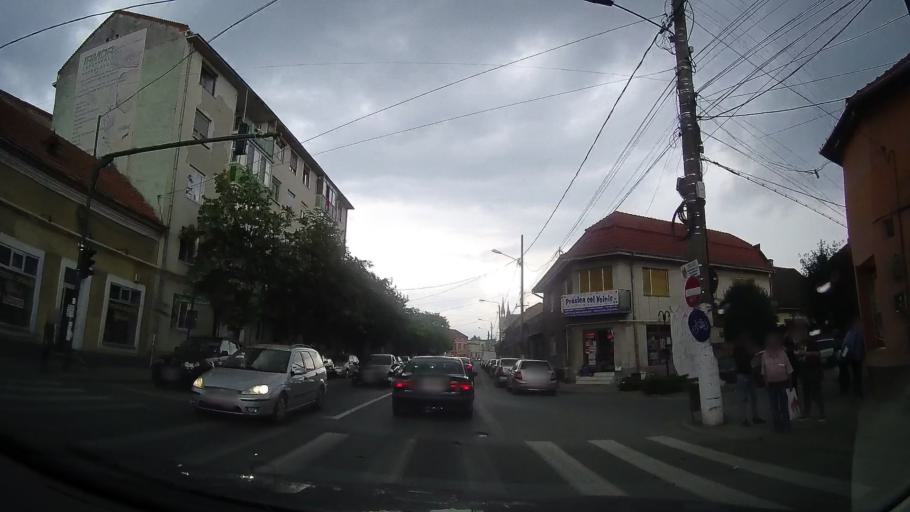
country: RO
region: Caras-Severin
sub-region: Municipiul Caransebes
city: Caransebes
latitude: 45.4104
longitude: 22.2174
